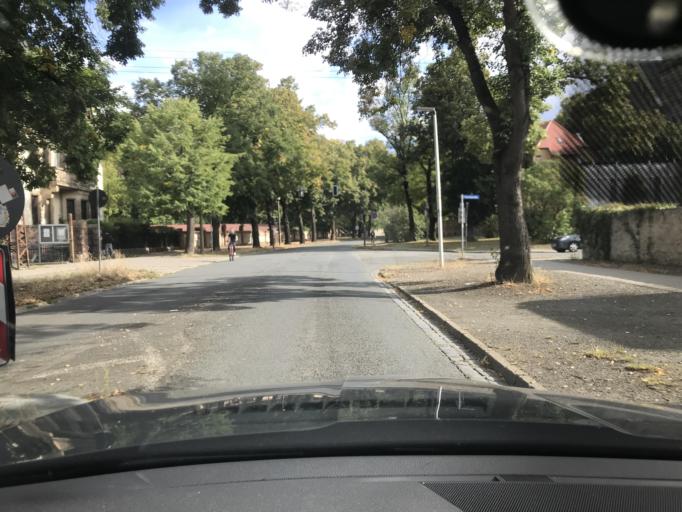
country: DE
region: Saxony-Anhalt
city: Quedlinburg
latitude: 51.7823
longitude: 11.1514
